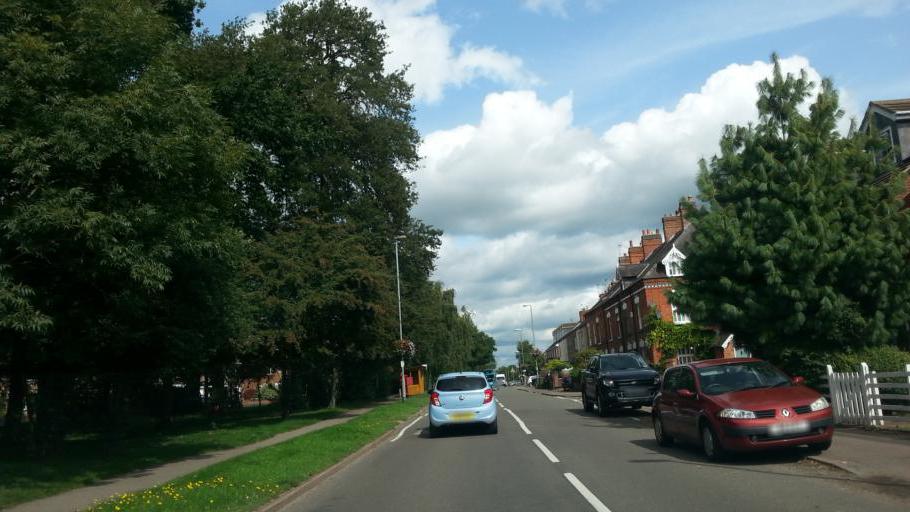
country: GB
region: England
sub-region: Leicestershire
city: Countesthorpe
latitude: 52.5559
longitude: -1.1360
